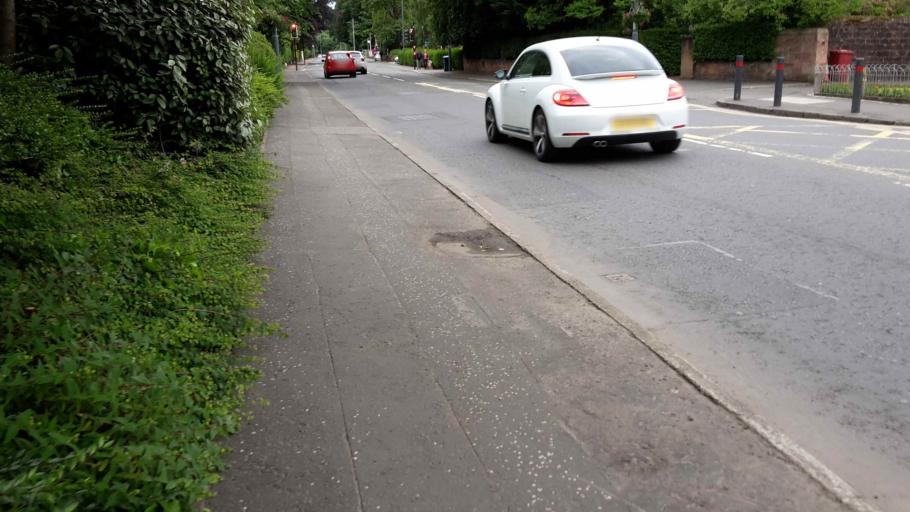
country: GB
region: Scotland
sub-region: South Lanarkshire
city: Uddingston
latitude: 55.8173
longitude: -4.0816
